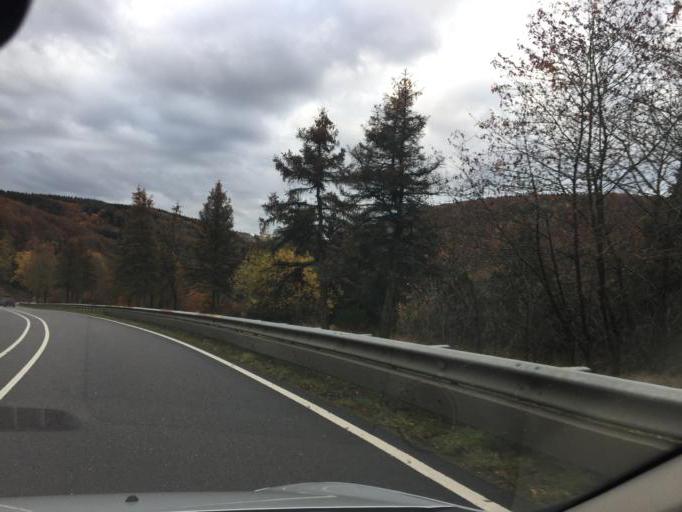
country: LU
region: Diekirch
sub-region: Canton de Wiltz
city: Esch-sur-Sure
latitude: 49.8958
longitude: 5.9563
